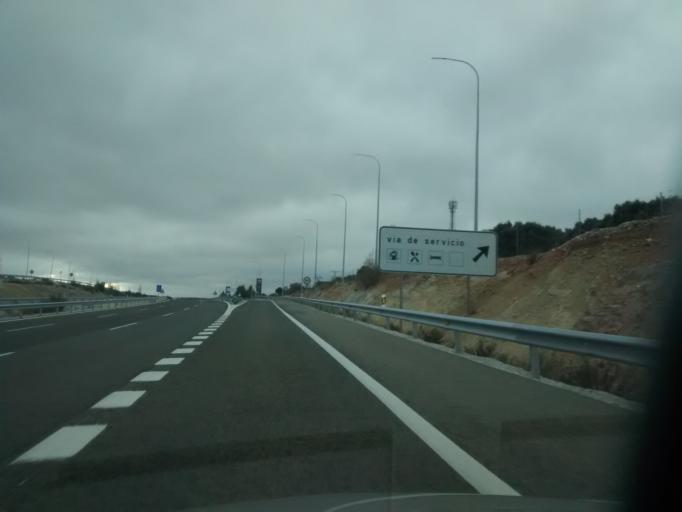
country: ES
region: Castille-La Mancha
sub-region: Provincia de Guadalajara
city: Sauca
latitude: 41.0148
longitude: -2.5517
